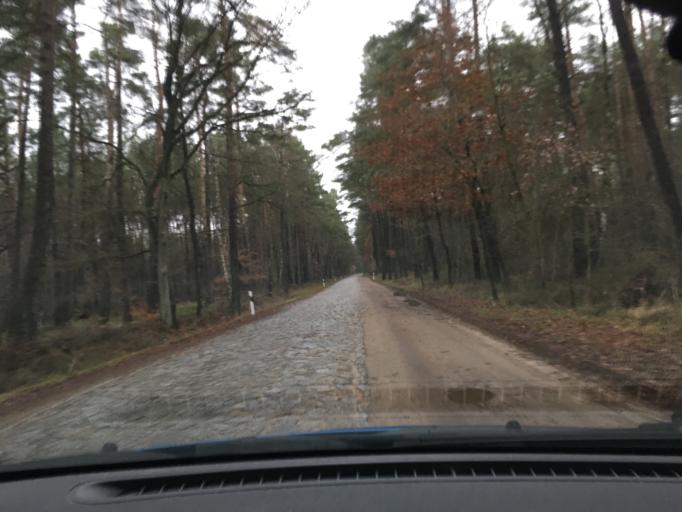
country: DE
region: Schleswig-Holstein
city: Brothen
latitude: 53.4387
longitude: 10.6988
